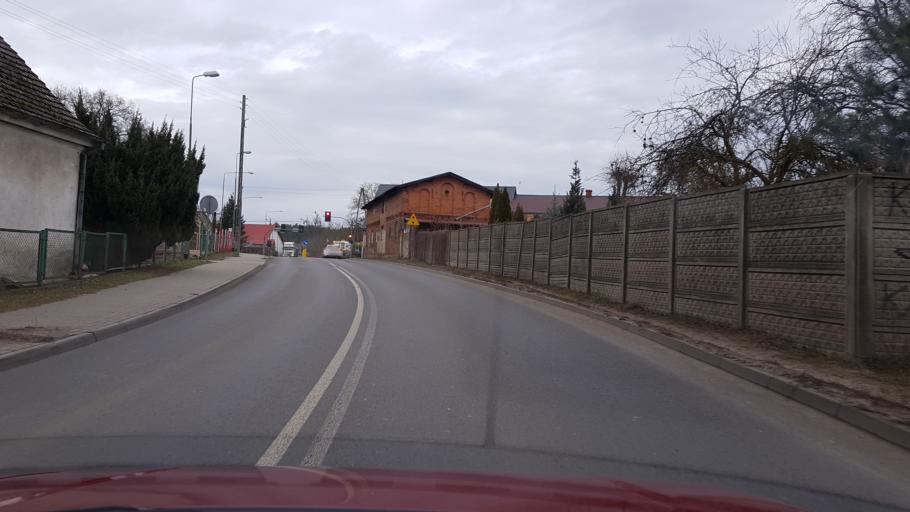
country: PL
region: West Pomeranian Voivodeship
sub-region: Powiat policki
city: Dobra
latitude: 53.4971
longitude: 14.4813
